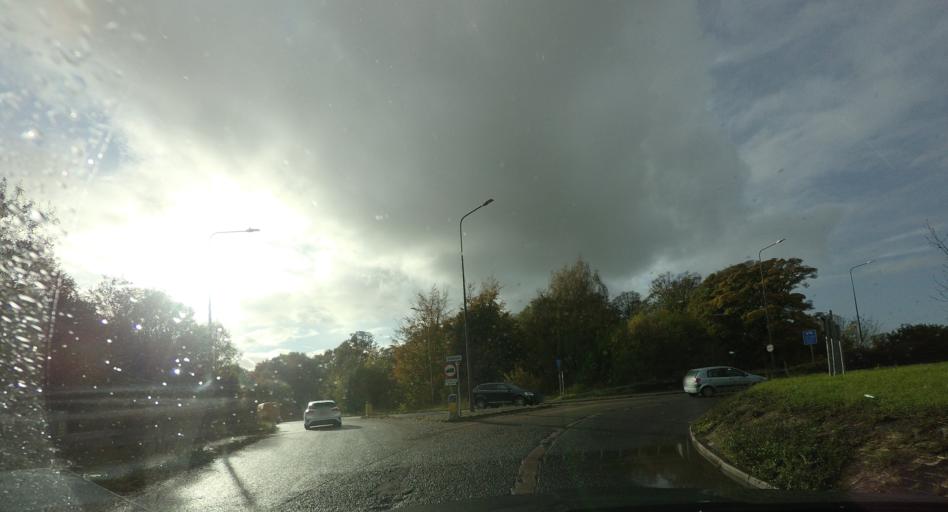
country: GB
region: England
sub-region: Medway
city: Cuxton
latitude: 51.4000
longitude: 0.4126
